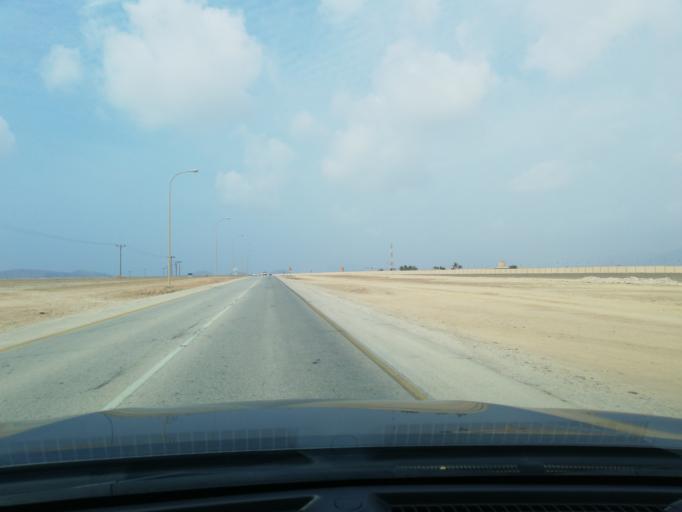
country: OM
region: Zufar
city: Salalah
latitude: 16.9426
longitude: 53.8476
